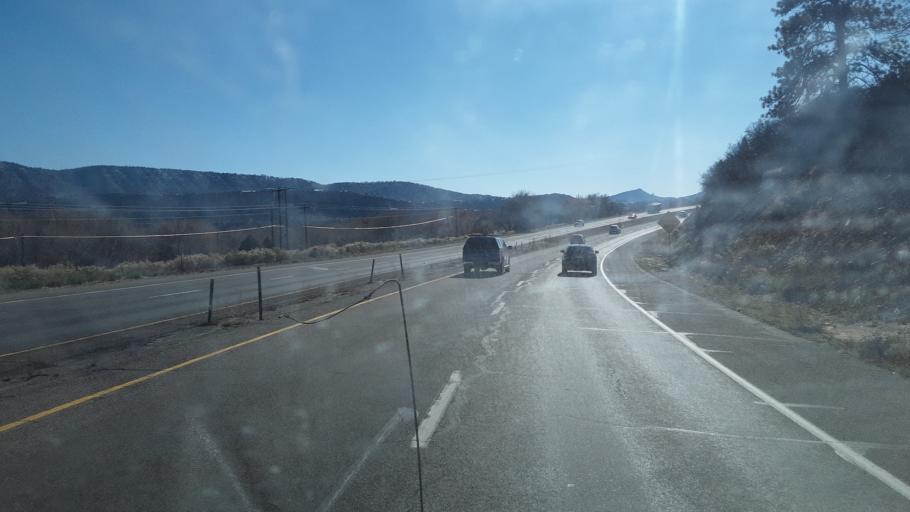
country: US
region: Colorado
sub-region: La Plata County
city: Durango
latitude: 37.3166
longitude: -107.8516
